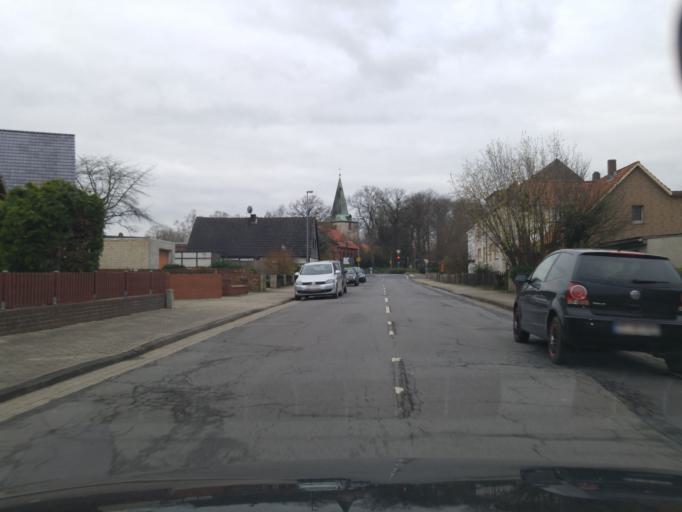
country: DE
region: Lower Saxony
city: Sohlde
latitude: 52.2100
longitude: 10.1764
